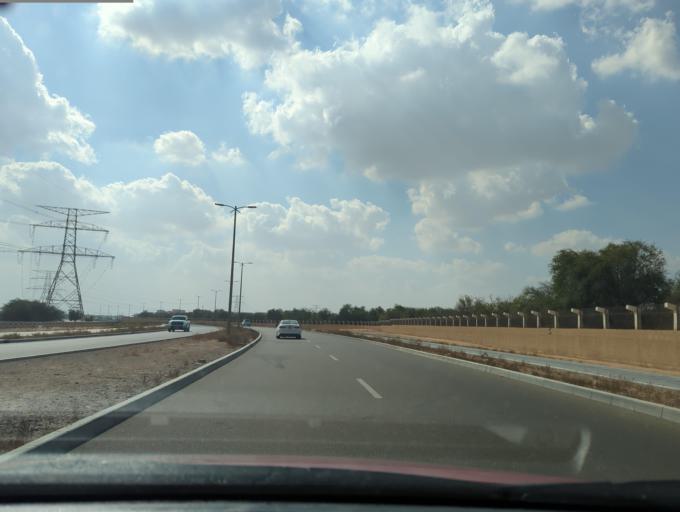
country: AE
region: Abu Dhabi
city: Al Ain
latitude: 24.1683
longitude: 55.6555
